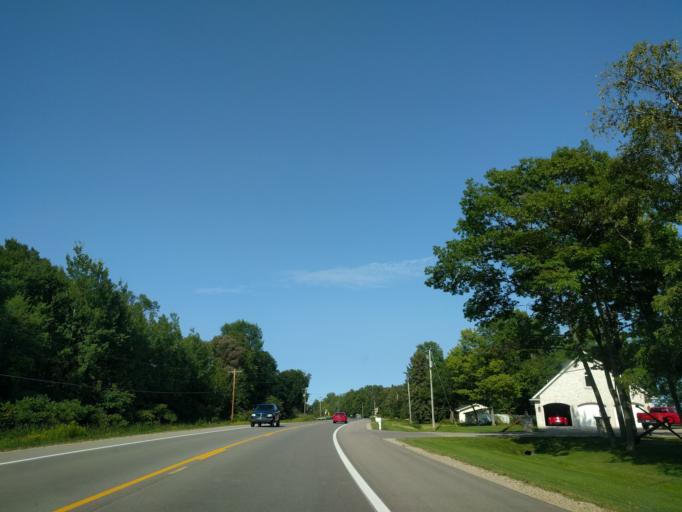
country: US
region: Michigan
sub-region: Menominee County
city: Menominee
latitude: 45.1511
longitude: -87.6008
